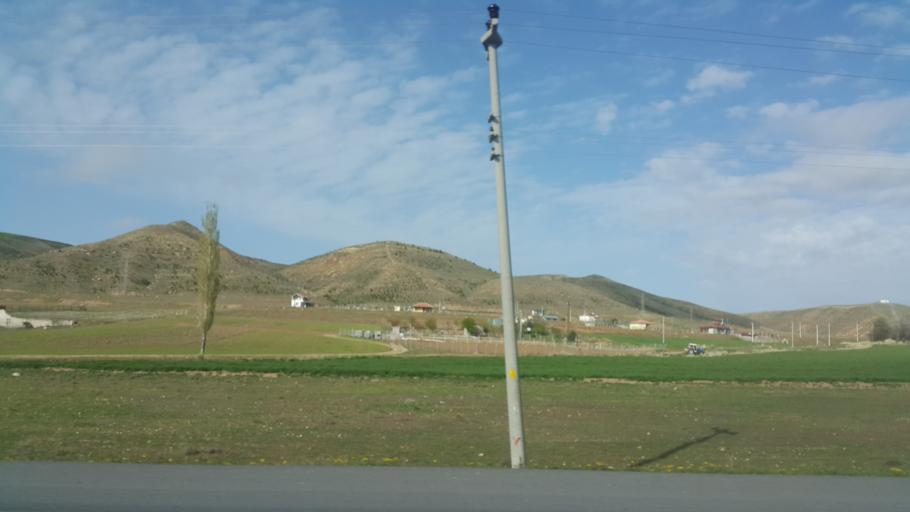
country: TR
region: Aksaray
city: Yesilova
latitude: 38.4408
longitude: 33.9409
